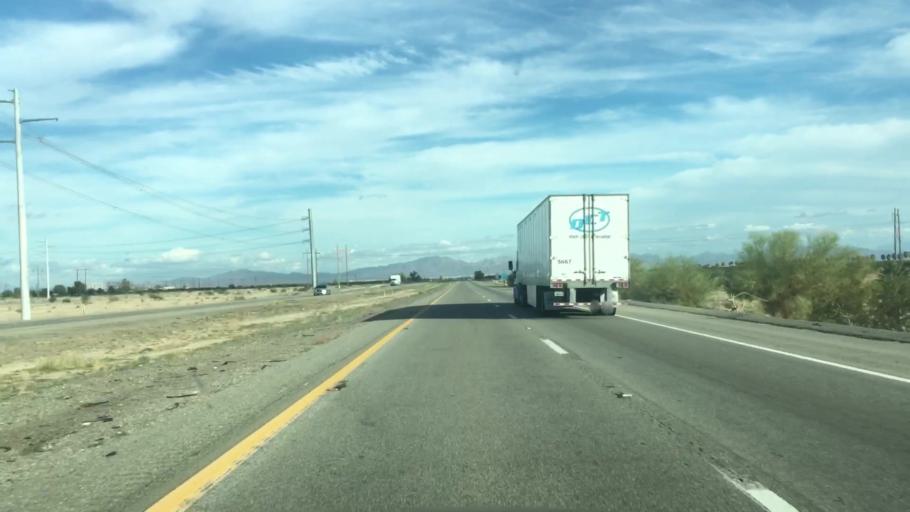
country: US
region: California
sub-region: Riverside County
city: Mesa Verde
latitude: 33.6066
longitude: -114.6954
